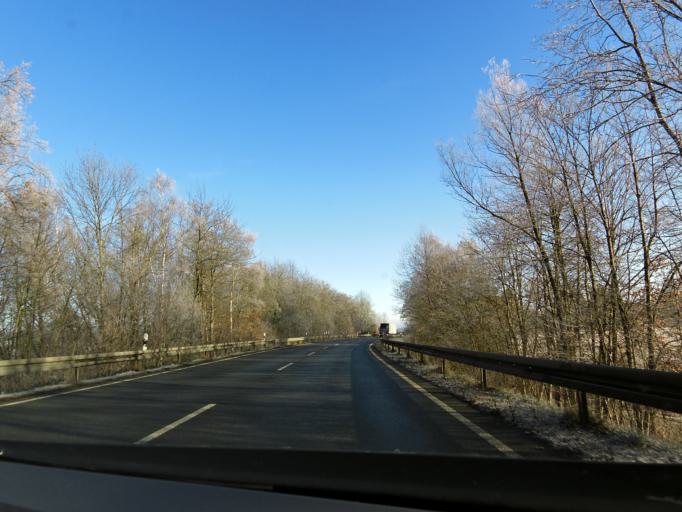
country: DE
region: Bavaria
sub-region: Upper Franconia
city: Marktredwitz
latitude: 50.0145
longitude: 12.0843
